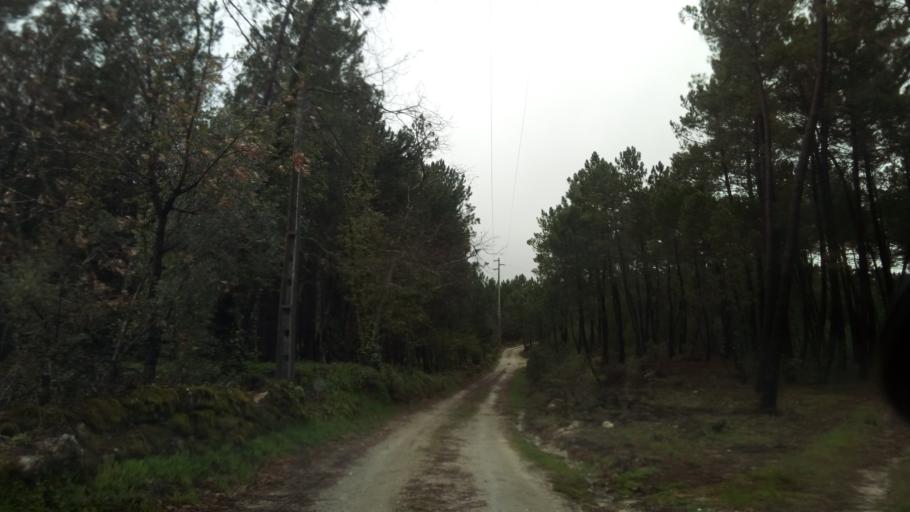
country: PT
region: Guarda
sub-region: Fornos de Algodres
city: Fornos de Algodres
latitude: 40.6216
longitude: -7.5231
